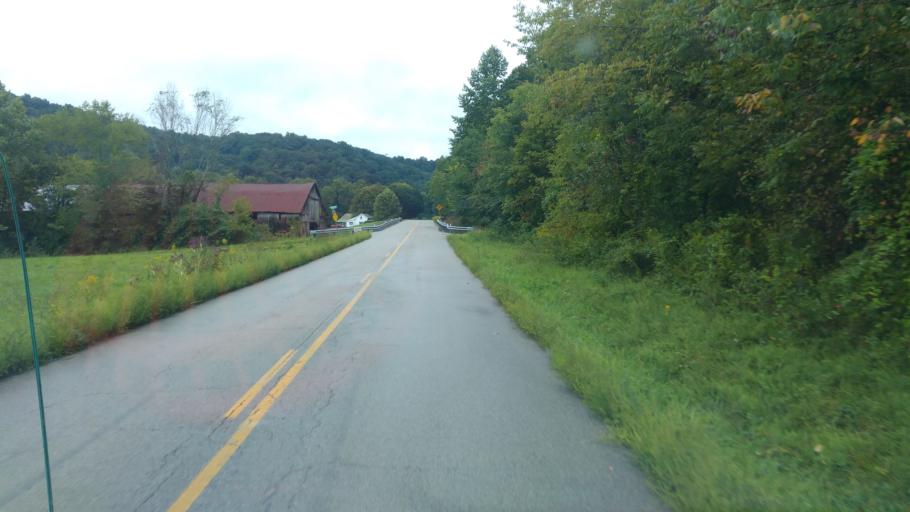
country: US
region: Kentucky
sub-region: Fleming County
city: Flemingsburg
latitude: 38.4304
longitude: -83.5027
